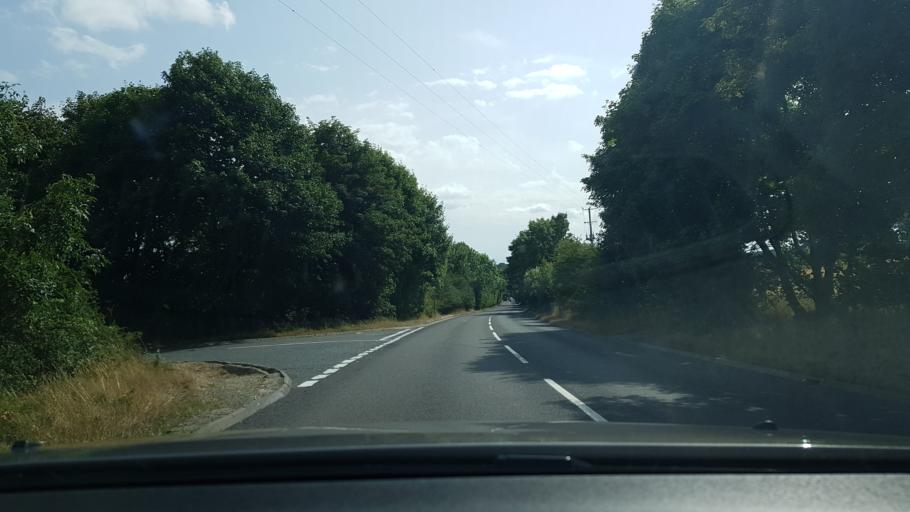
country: GB
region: England
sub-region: West Berkshire
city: Hungerford
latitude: 51.4476
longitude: -1.4854
